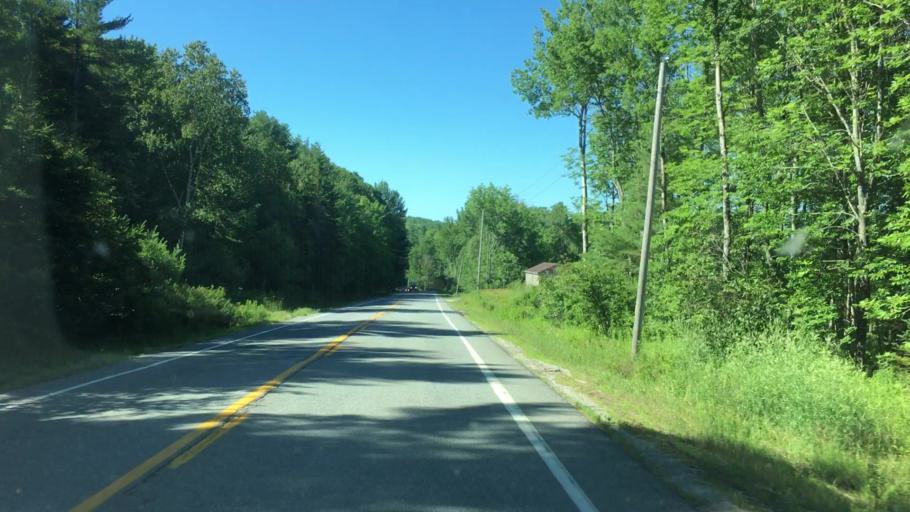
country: US
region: Maine
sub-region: Hancock County
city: Dedham
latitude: 44.6678
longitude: -68.6739
